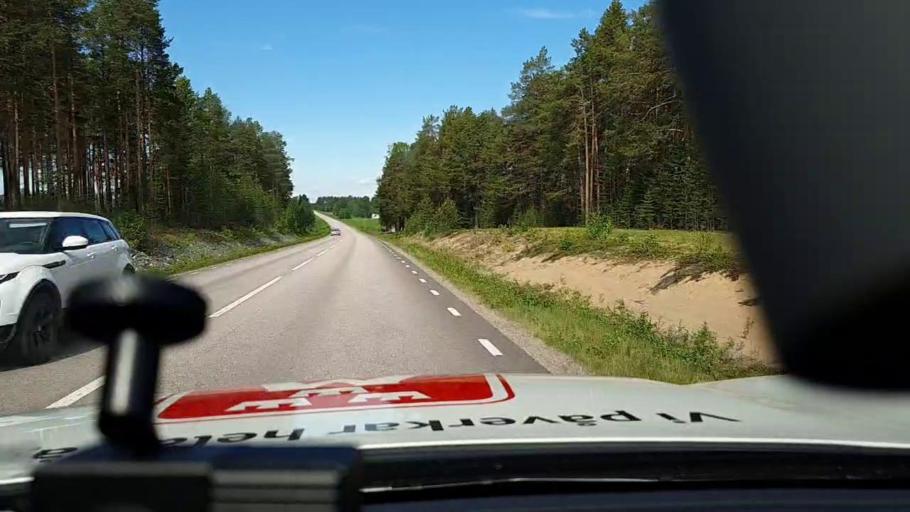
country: SE
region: Norrbotten
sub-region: Lulea Kommun
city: Sodra Sunderbyn
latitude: 65.6359
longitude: 21.9163
